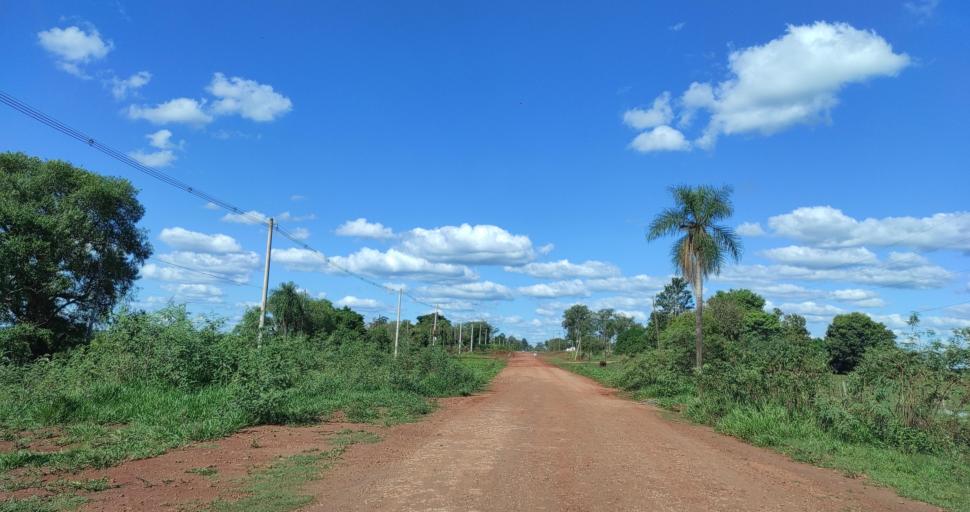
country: AR
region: Misiones
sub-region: Departamento de Candelaria
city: Candelaria
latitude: -27.4634
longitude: -55.7271
